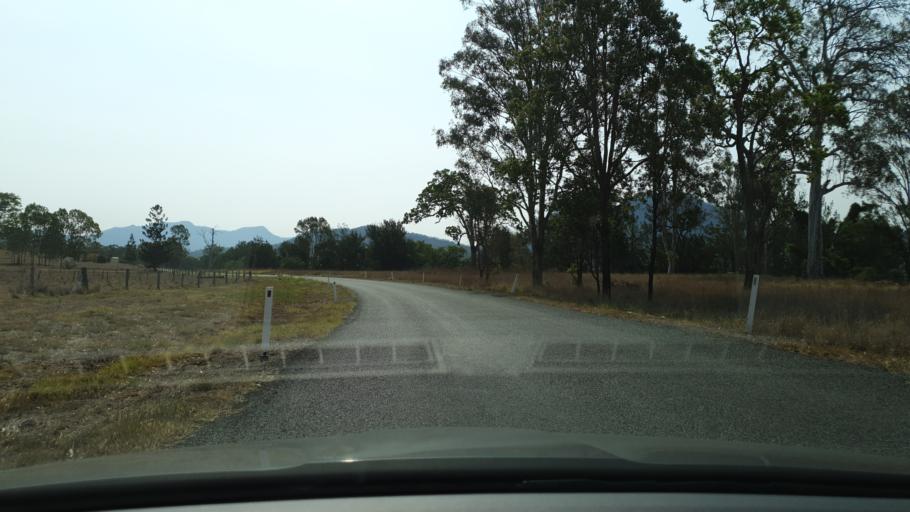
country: AU
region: Queensland
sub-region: Ipswich
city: Deebing Heights
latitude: -28.1370
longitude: 152.5944
